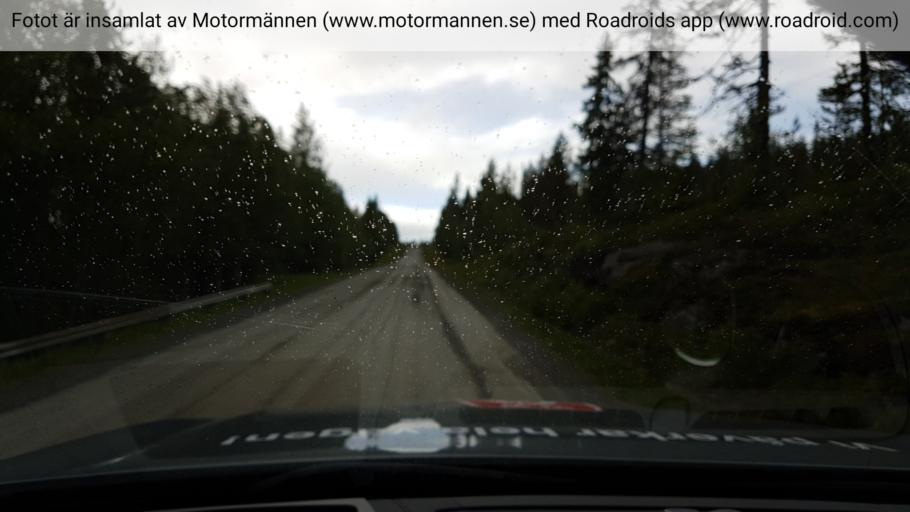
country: NO
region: Nord-Trondelag
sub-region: Snasa
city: Snaase
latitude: 63.7296
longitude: 12.5369
